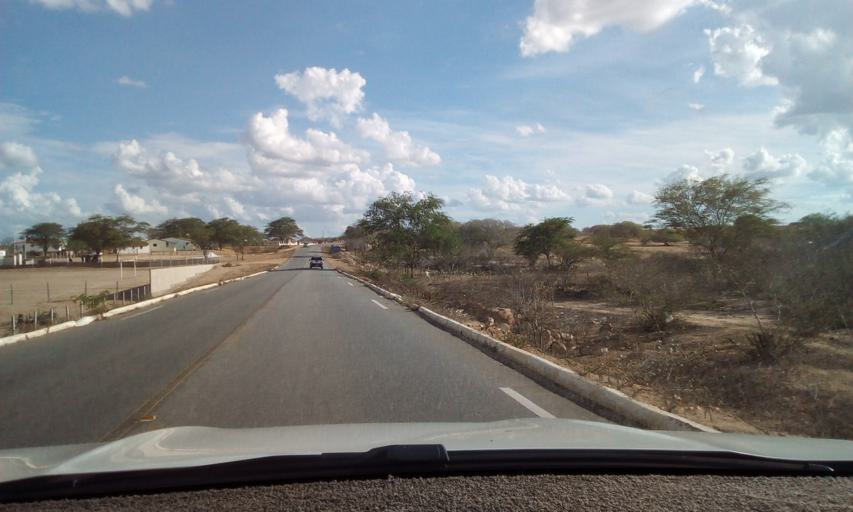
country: BR
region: Paraiba
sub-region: Soledade
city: Soledade
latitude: -6.9205
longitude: -36.3857
